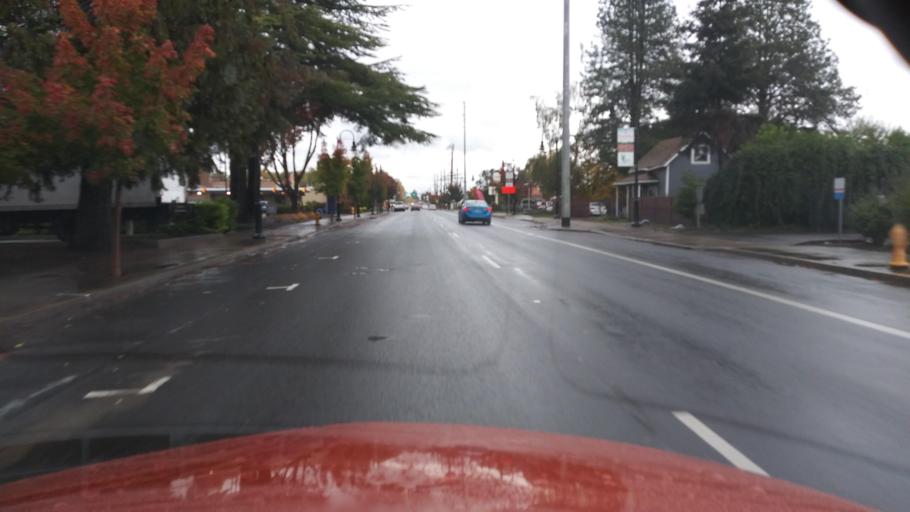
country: US
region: Oregon
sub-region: Washington County
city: Cornelius
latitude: 45.5201
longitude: -123.0513
